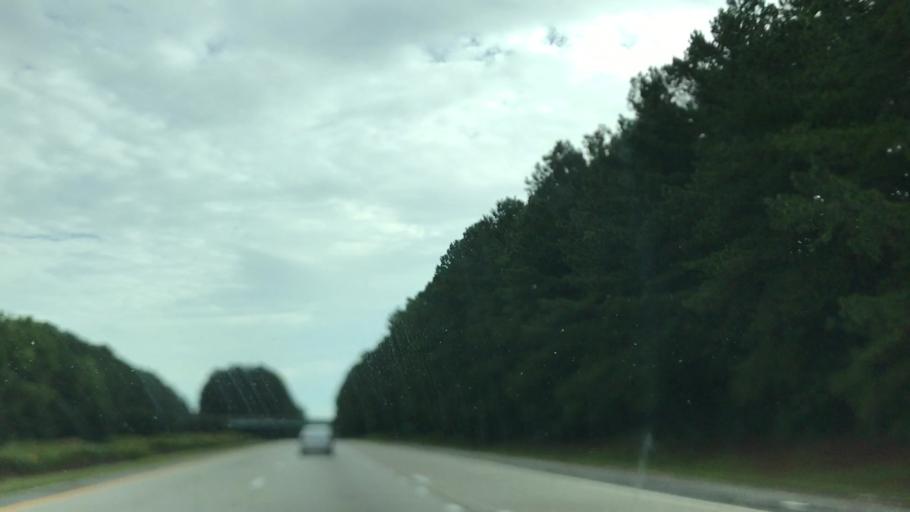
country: US
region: North Carolina
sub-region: Nash County
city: Red Oak
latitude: 35.9919
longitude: -77.8731
